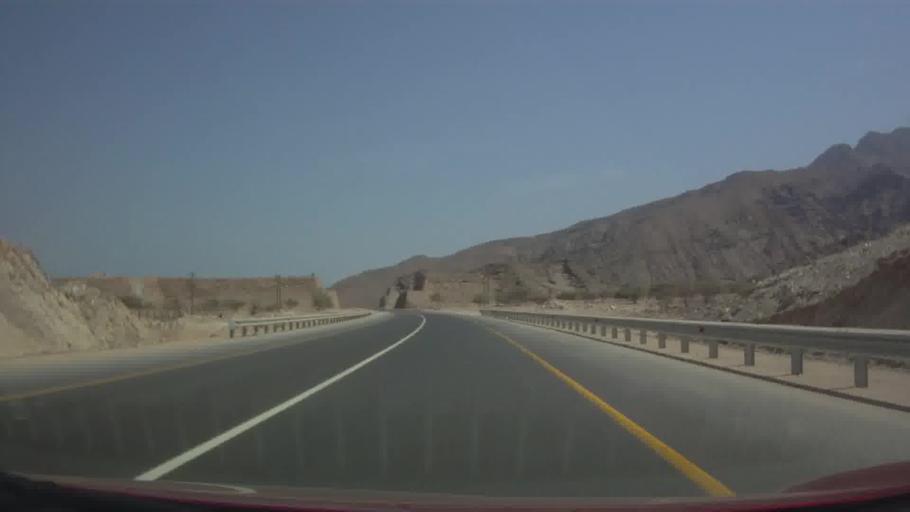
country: OM
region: Muhafazat Masqat
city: Muscat
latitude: 23.3957
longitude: 58.7851
